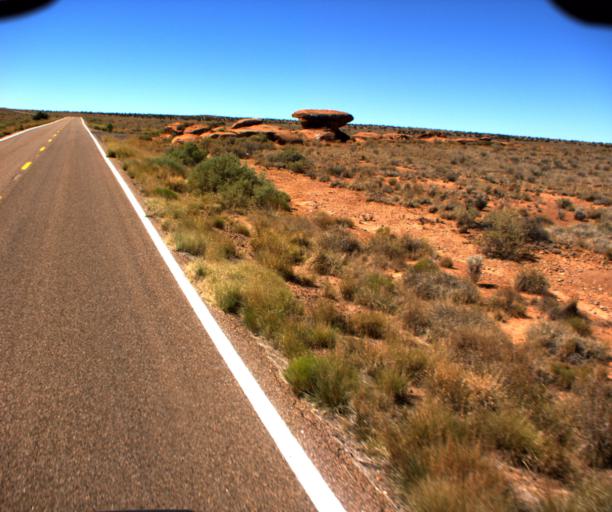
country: US
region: Arizona
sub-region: Navajo County
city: Winslow
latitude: 34.9481
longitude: -110.6459
